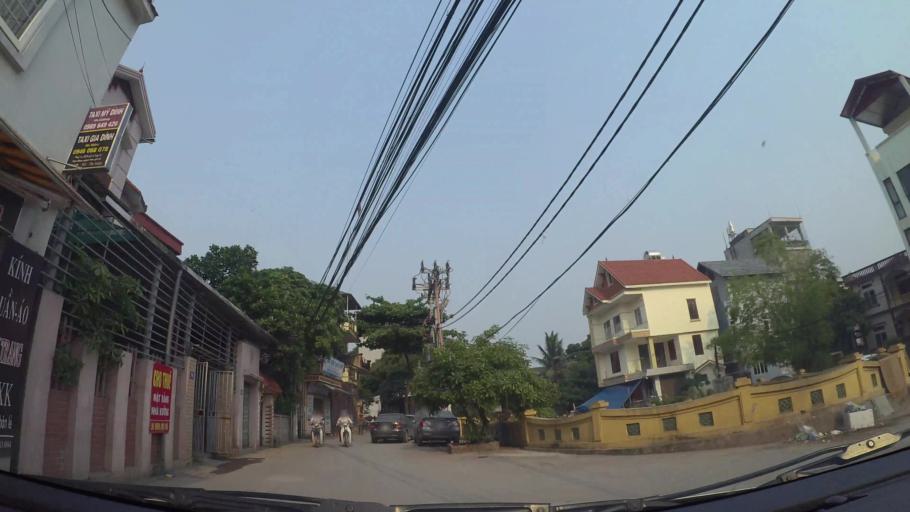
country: VN
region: Ha Noi
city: Cau Dien
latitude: 21.0016
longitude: 105.7473
